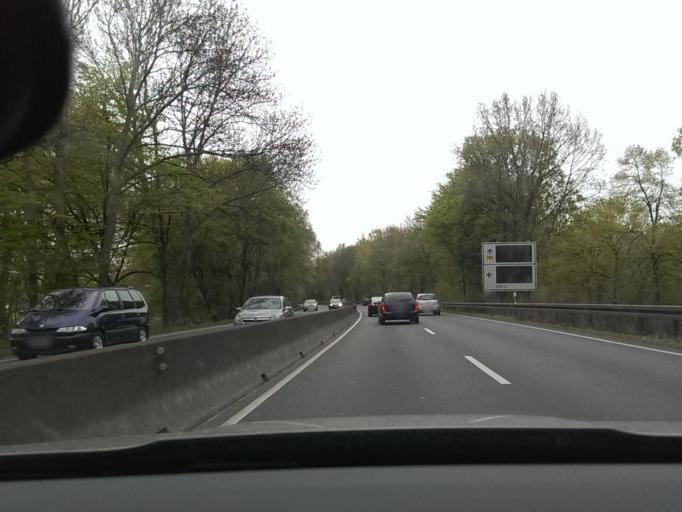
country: DE
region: Lower Saxony
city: Hannover
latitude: 52.3844
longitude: 9.6907
